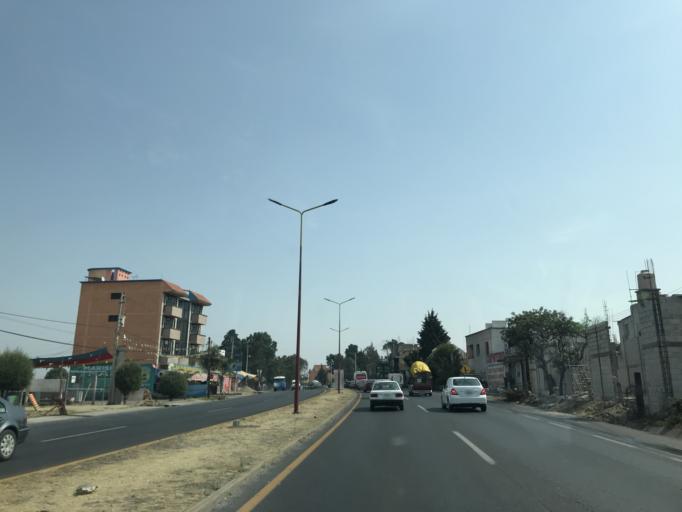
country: MX
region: Tlaxcala
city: La Magdalena Tlaltelulco
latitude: 19.2738
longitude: -98.1970
